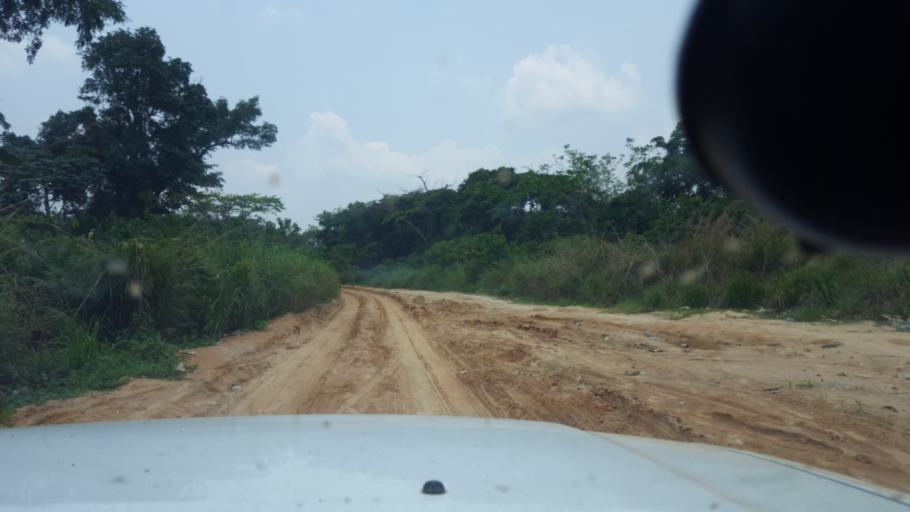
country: CD
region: Bandundu
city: Mushie
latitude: -3.7542
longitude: 16.6275
